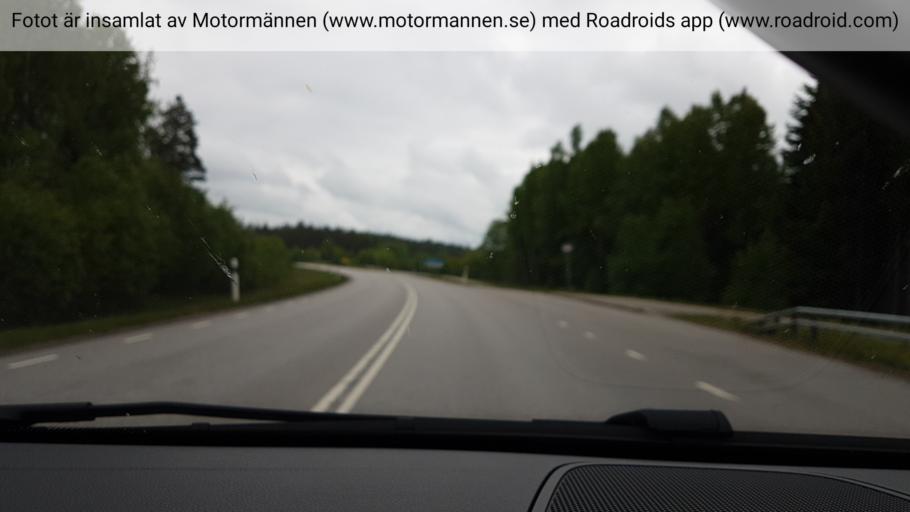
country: SE
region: Uppsala
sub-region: Osthammars Kommun
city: Bjorklinge
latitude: 60.0116
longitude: 17.5891
